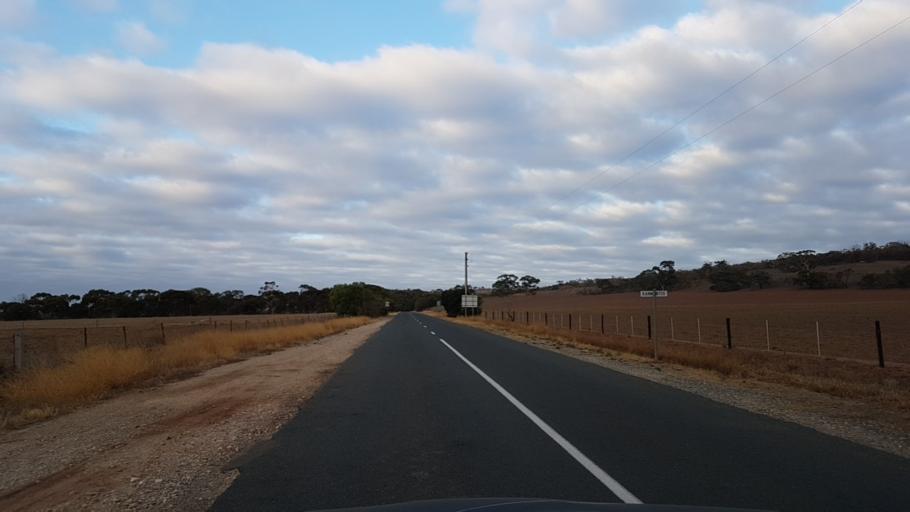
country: AU
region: South Australia
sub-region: Mount Barker
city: Callington
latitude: -35.0814
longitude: 139.0128
